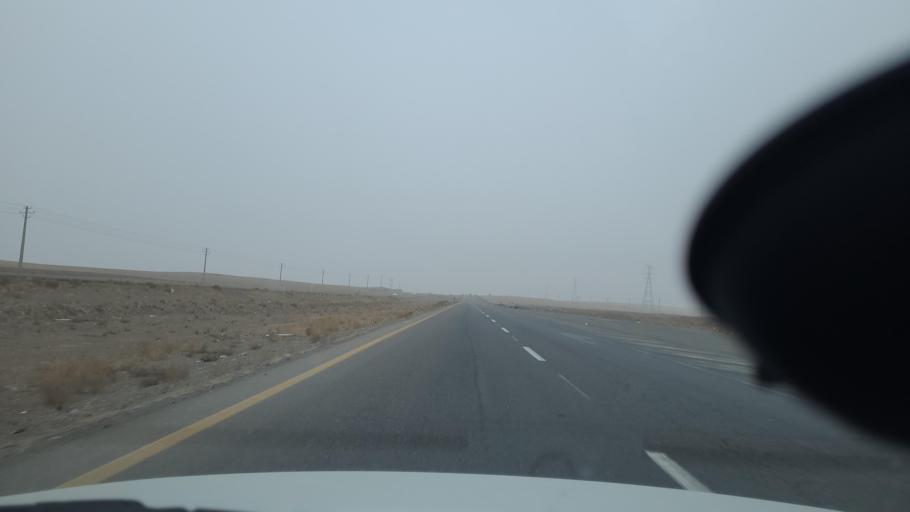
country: IR
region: Razavi Khorasan
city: Fariman
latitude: 35.8889
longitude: 59.7590
